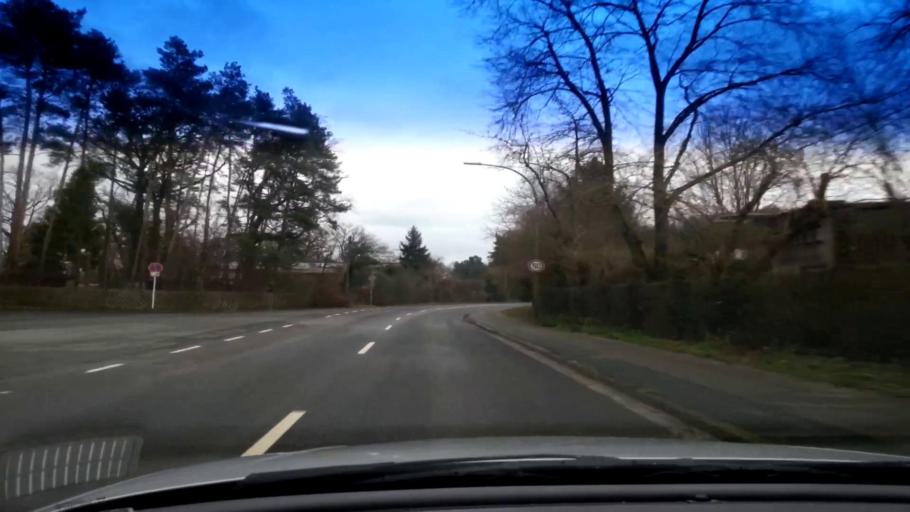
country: DE
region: Bavaria
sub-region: Upper Franconia
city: Pettstadt
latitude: 49.8609
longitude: 10.9158
